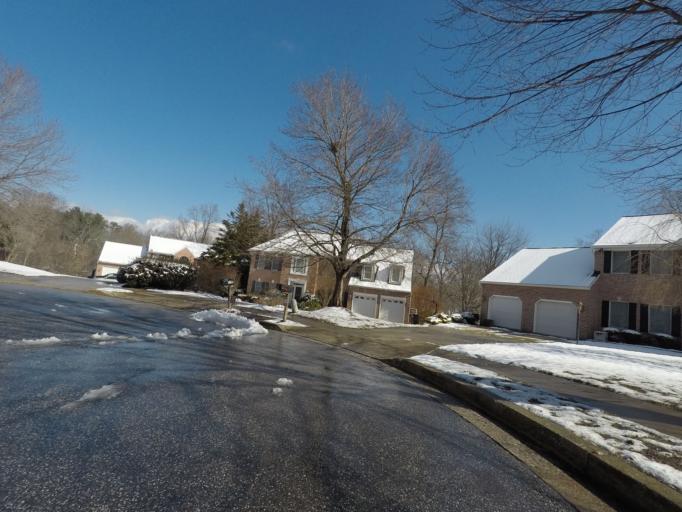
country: US
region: Maryland
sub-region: Howard County
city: Columbia
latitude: 39.2677
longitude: -76.8526
